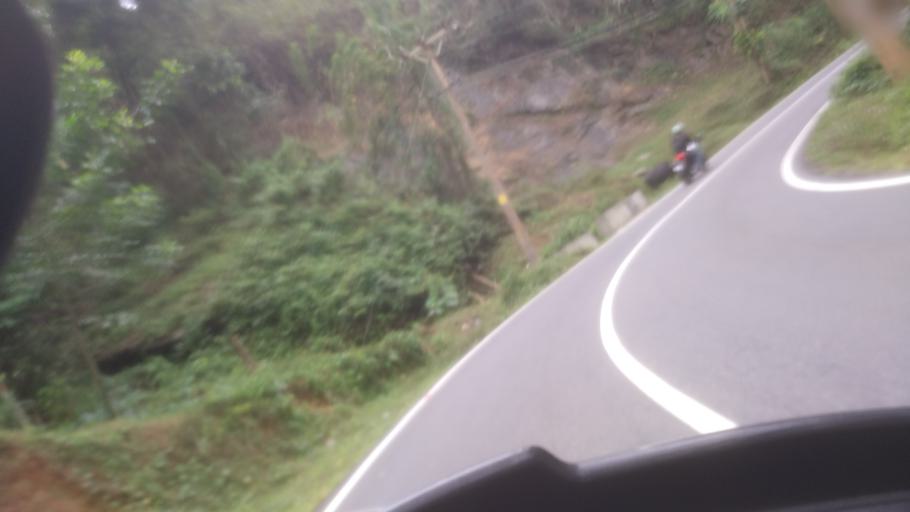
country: IN
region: Kerala
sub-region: Idukki
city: Idukki
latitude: 9.9642
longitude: 77.0025
